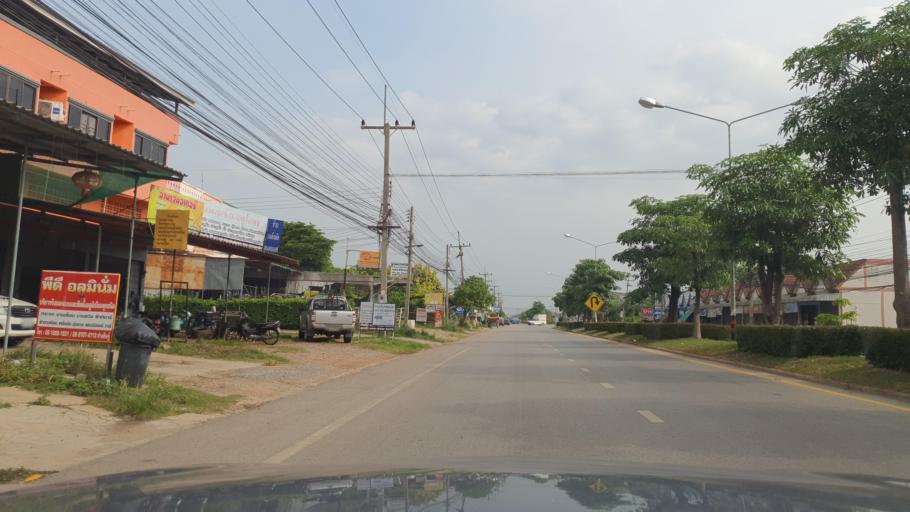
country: TH
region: Phitsanulok
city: Phitsanulok
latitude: 16.8578
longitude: 100.2525
